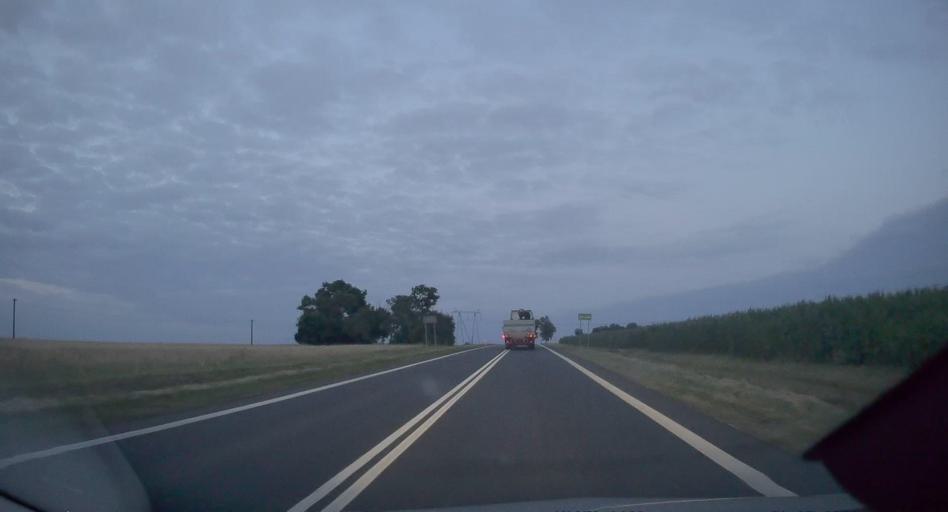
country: PL
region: Silesian Voivodeship
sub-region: Powiat klobucki
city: Opatow
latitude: 50.9507
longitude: 18.8215
